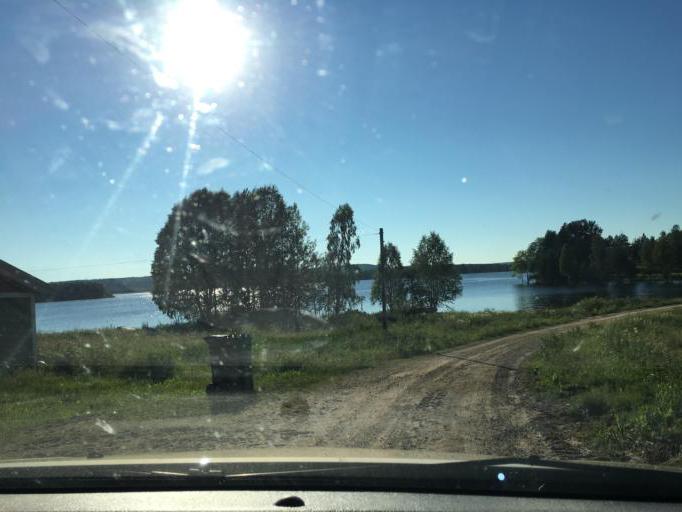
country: SE
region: Norrbotten
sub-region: Overkalix Kommun
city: OEverkalix
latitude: 66.1066
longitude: 22.7812
